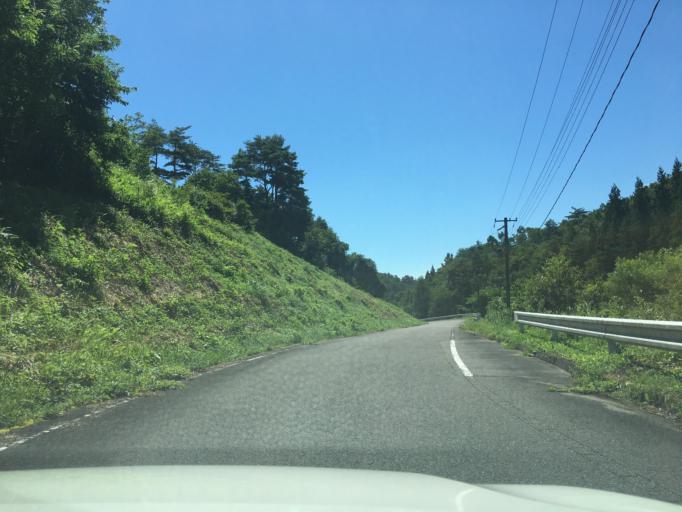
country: JP
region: Fukushima
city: Ishikawa
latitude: 37.2182
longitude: 140.5236
